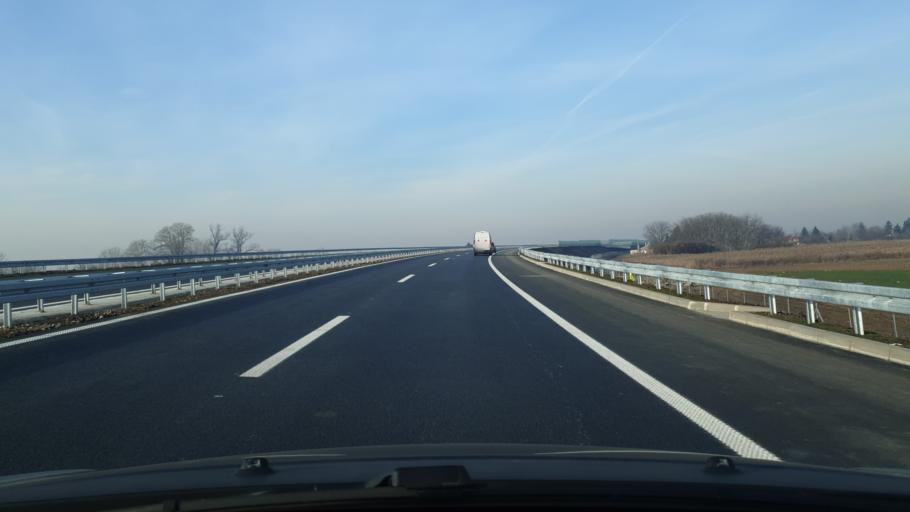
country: RS
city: Boljevci
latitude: 44.7292
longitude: 20.2477
